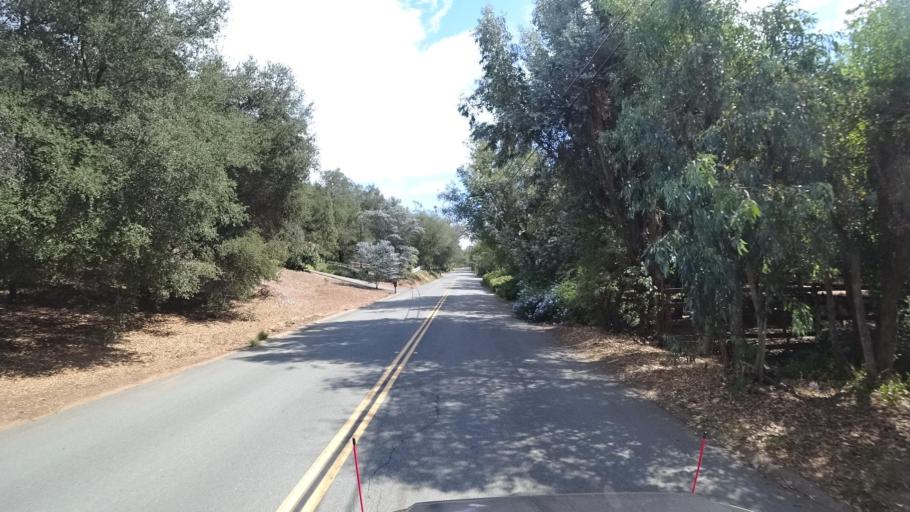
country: US
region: California
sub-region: San Diego County
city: Valley Center
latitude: 33.2009
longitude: -117.0358
